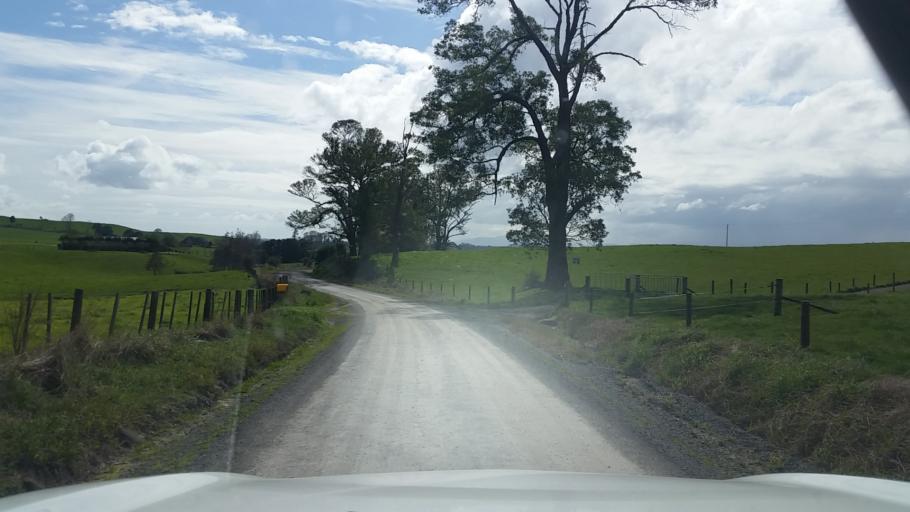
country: NZ
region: Waikato
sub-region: Hauraki District
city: Ngatea
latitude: -37.4542
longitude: 175.5007
